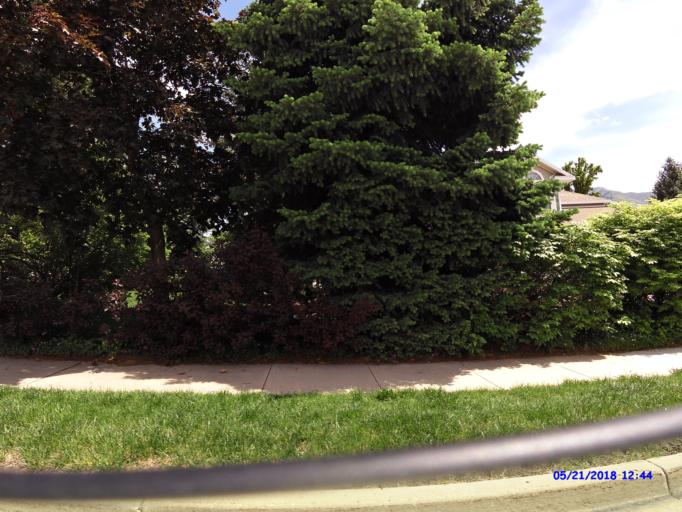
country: US
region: Utah
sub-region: Weber County
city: Washington Terrace
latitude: 41.1748
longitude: -111.9548
